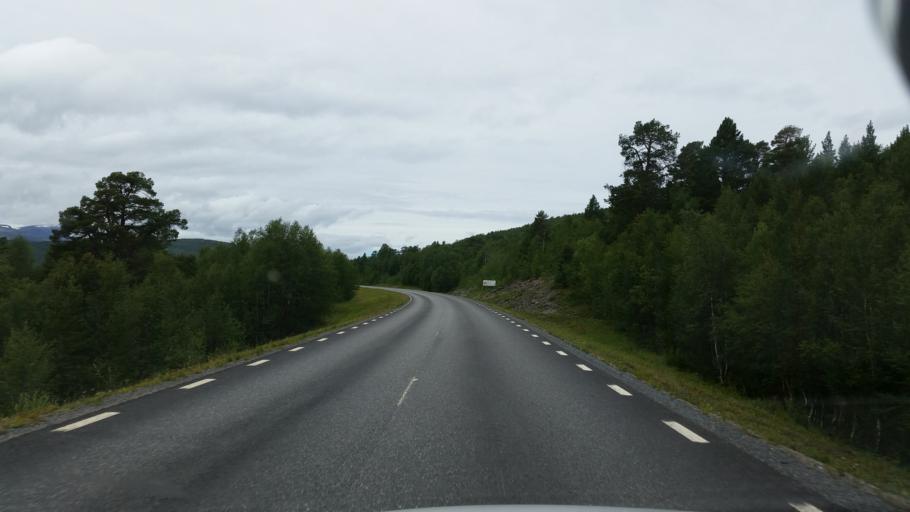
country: NO
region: Nordland
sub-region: Sorfold
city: Straumen
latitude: 66.5234
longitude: 16.3726
